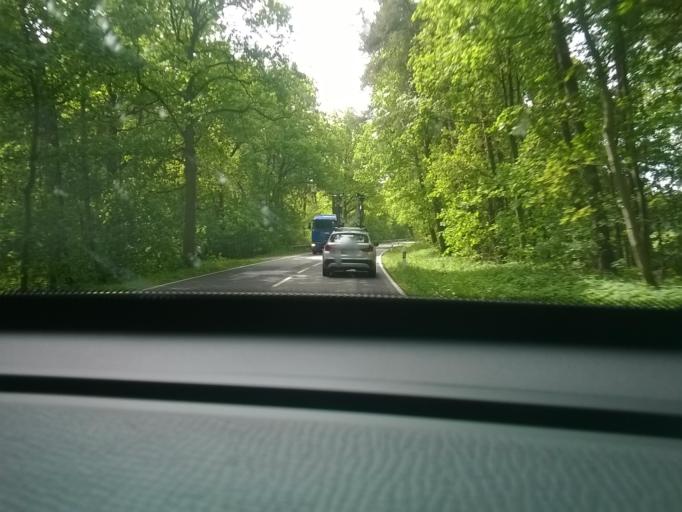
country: DE
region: Brandenburg
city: Wittstock
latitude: 53.0898
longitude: 12.4843
